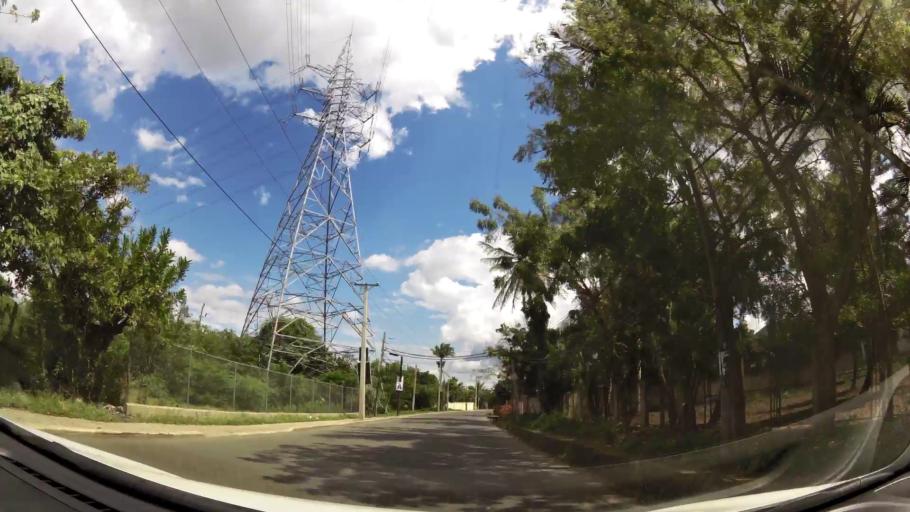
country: DO
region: Santiago
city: Licey al Medio
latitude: 19.4008
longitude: -70.6524
